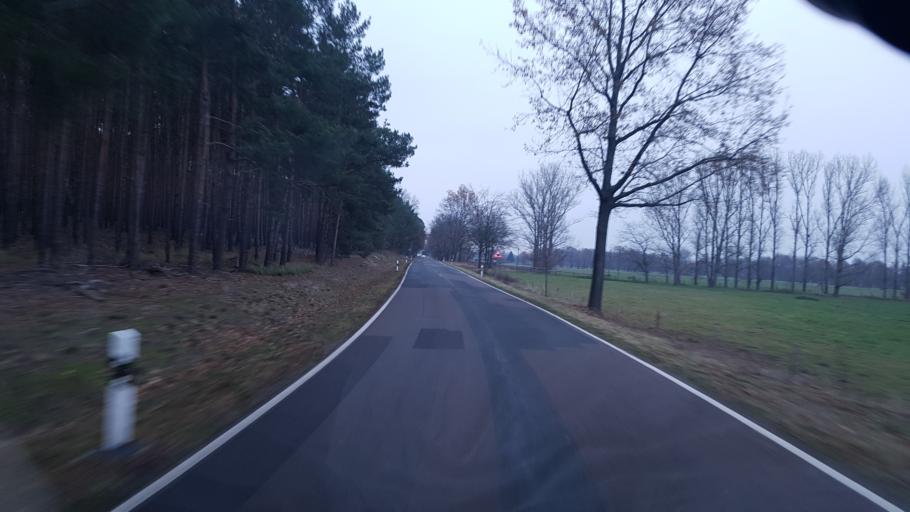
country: DE
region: Brandenburg
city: Briesen
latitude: 51.8517
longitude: 14.2326
